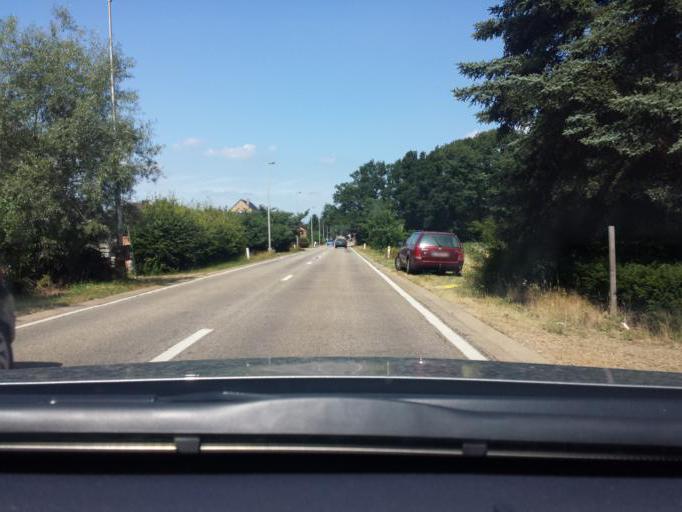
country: BE
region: Flanders
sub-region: Provincie Limburg
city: Lummen
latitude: 51.0012
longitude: 5.1389
